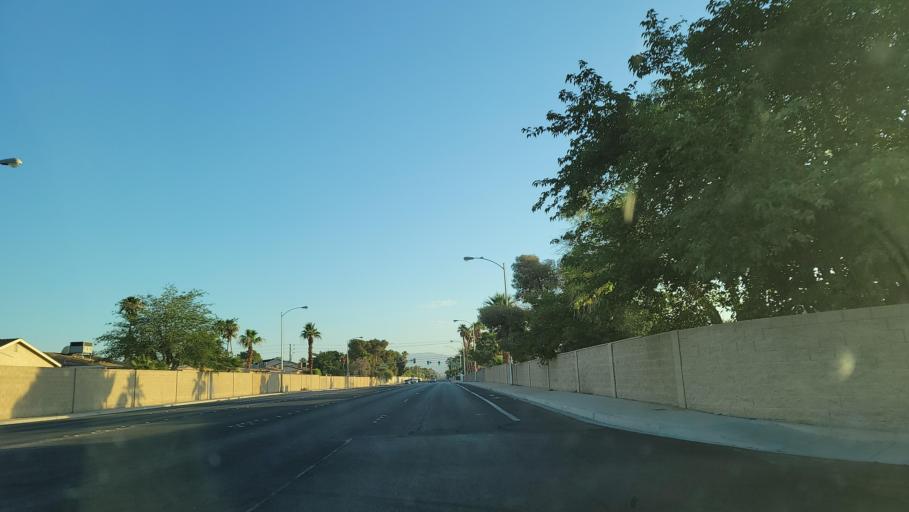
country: US
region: Nevada
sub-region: Clark County
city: Spring Valley
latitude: 36.1236
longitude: -115.2339
